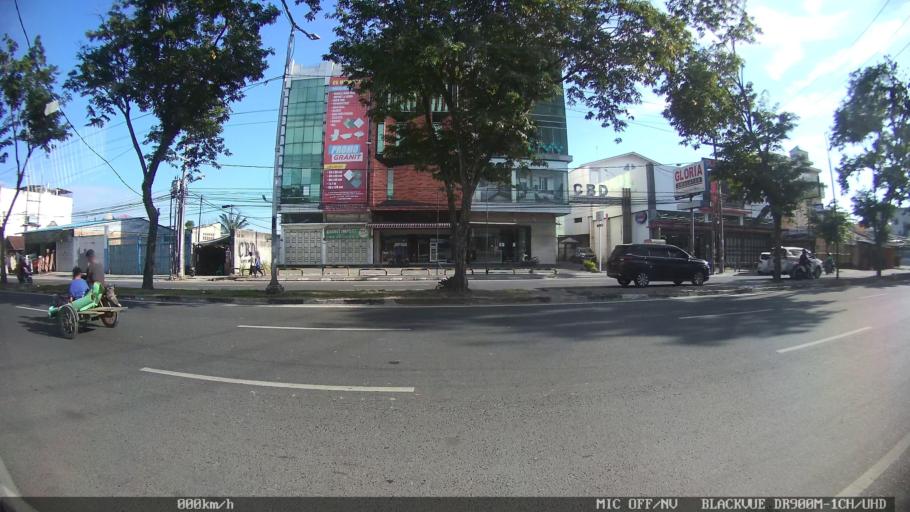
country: ID
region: North Sumatra
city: Medan
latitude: 3.5902
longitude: 98.6510
